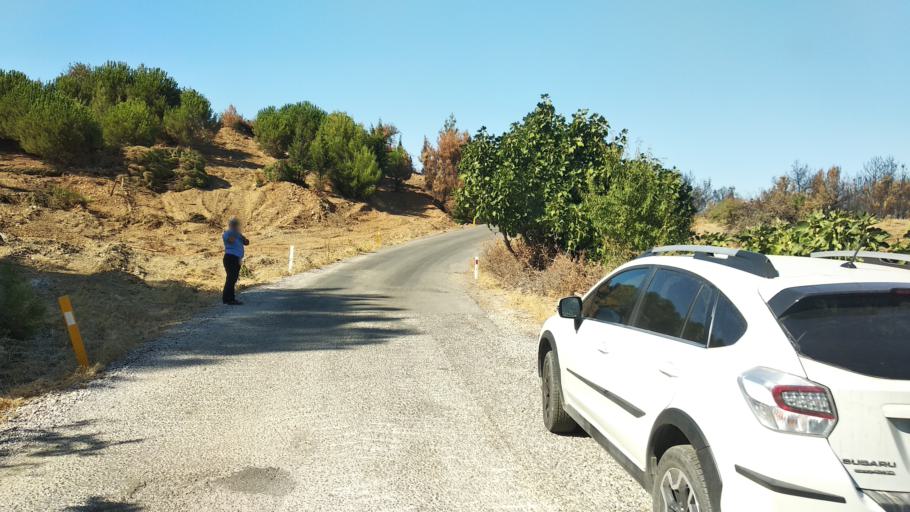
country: TR
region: Izmir
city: Gaziemir
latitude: 38.2891
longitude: 27.0018
